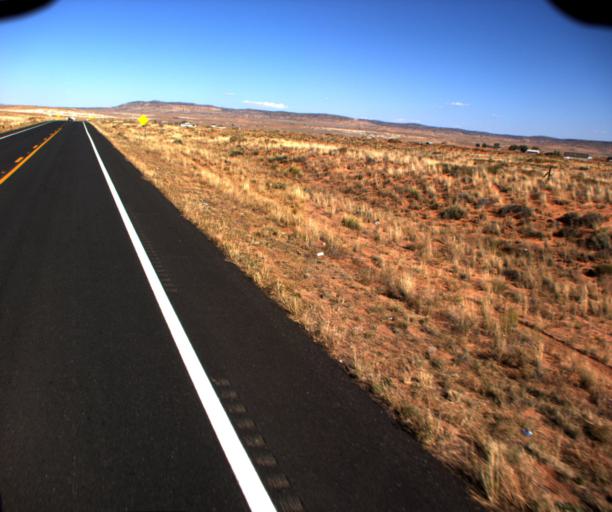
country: US
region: Arizona
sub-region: Coconino County
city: Kaibito
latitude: 36.3138
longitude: -110.9565
